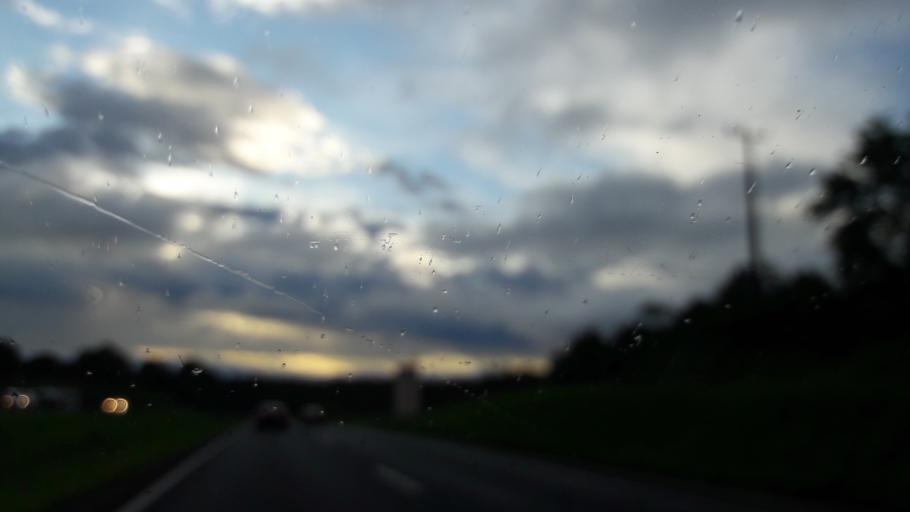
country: BR
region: Parana
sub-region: Campina Grande Do Sul
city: Campina Grande do Sul
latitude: -25.1757
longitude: -48.8719
